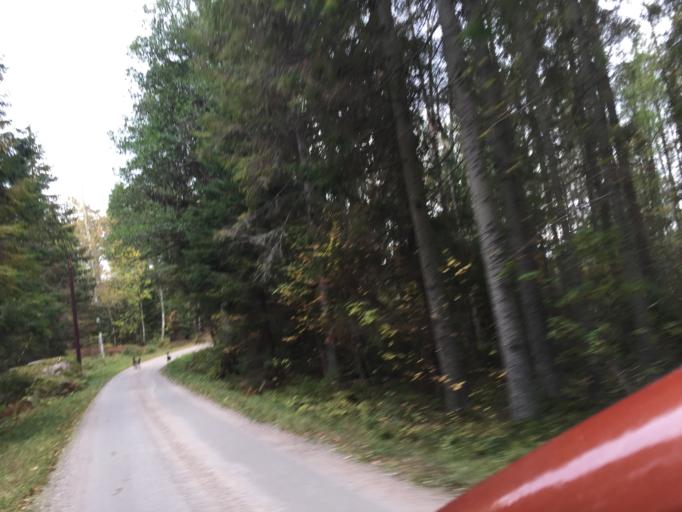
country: SE
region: Soedermanland
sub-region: Vingakers Kommun
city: Vingaker
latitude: 59.0186
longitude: 15.7787
